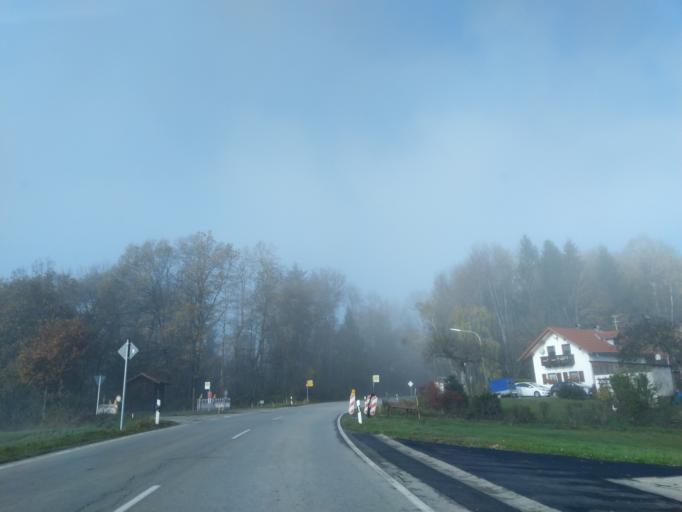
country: DE
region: Bavaria
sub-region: Lower Bavaria
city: Aussernzell
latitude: 48.7214
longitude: 13.2322
